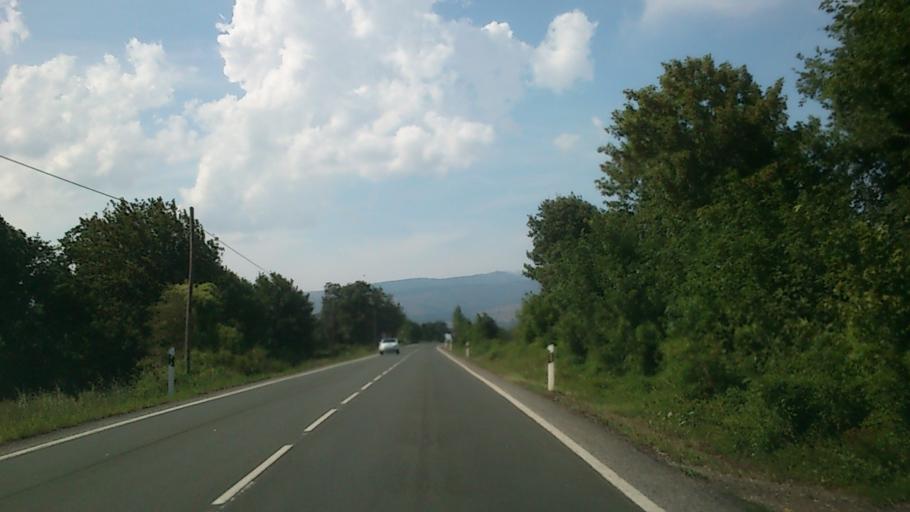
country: ES
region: Castille and Leon
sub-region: Provincia de Burgos
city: Espinosa de los Monteros
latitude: 43.0527
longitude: -3.4896
